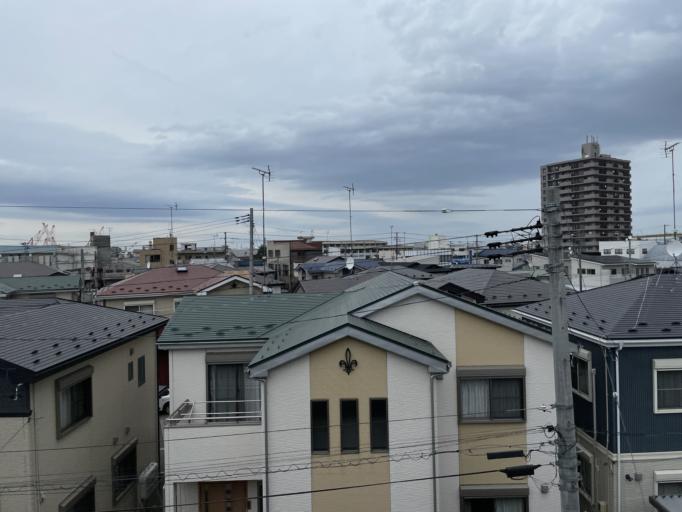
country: JP
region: Aomori
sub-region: Hachinohe Shi
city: Uchimaru
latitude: 40.5188
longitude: 141.5105
